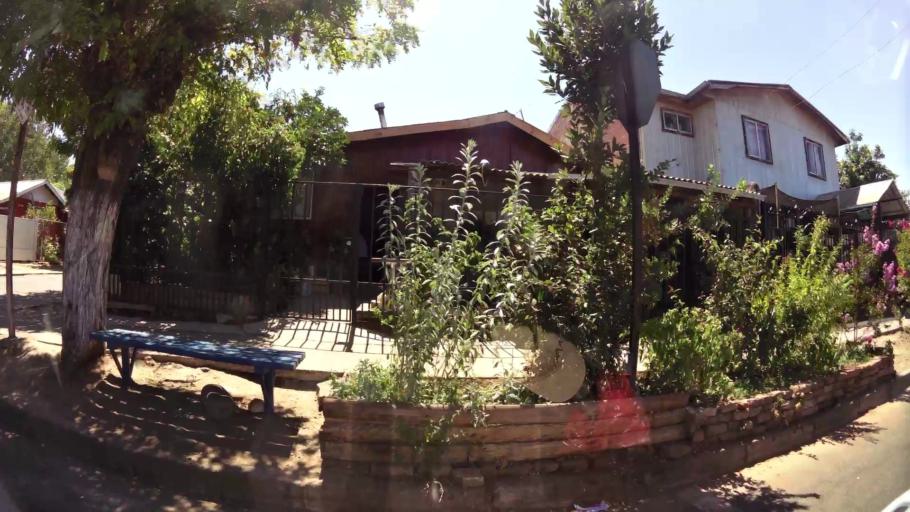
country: CL
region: Maule
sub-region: Provincia de Talca
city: Talca
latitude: -35.3071
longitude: -71.5147
